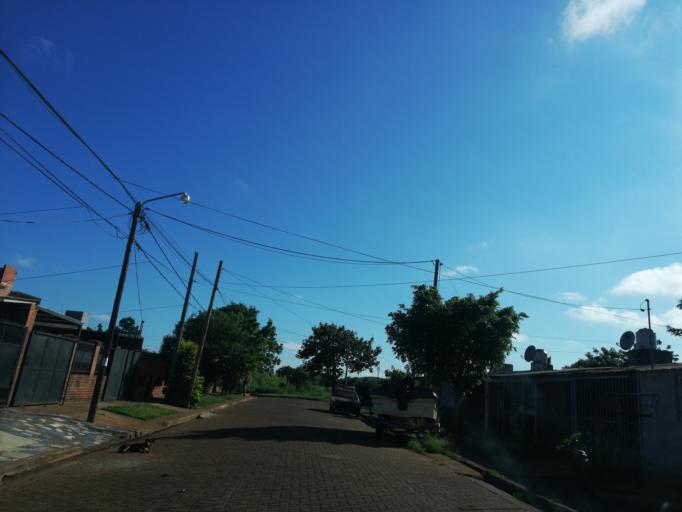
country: AR
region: Misiones
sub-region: Departamento de Capital
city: Posadas
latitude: -27.4250
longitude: -55.9383
